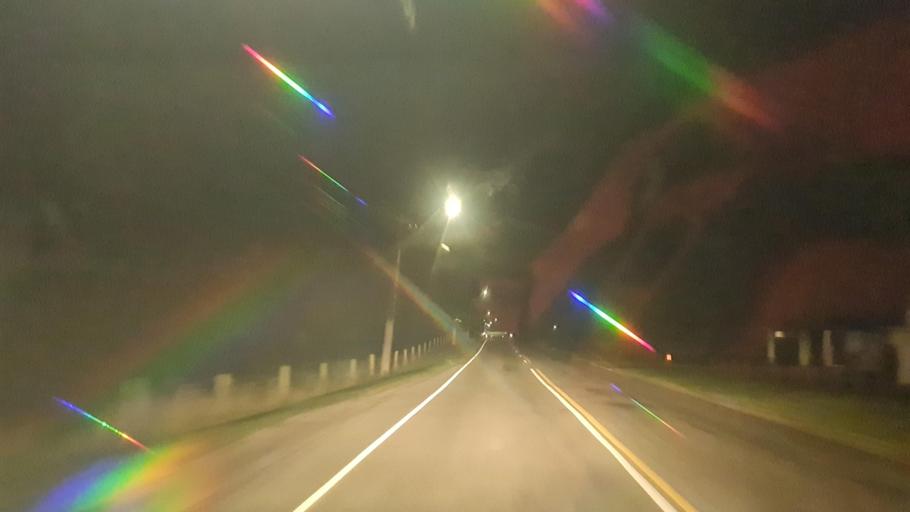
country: NZ
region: Otago
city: Oamaru
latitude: -45.1007
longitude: 170.9421
